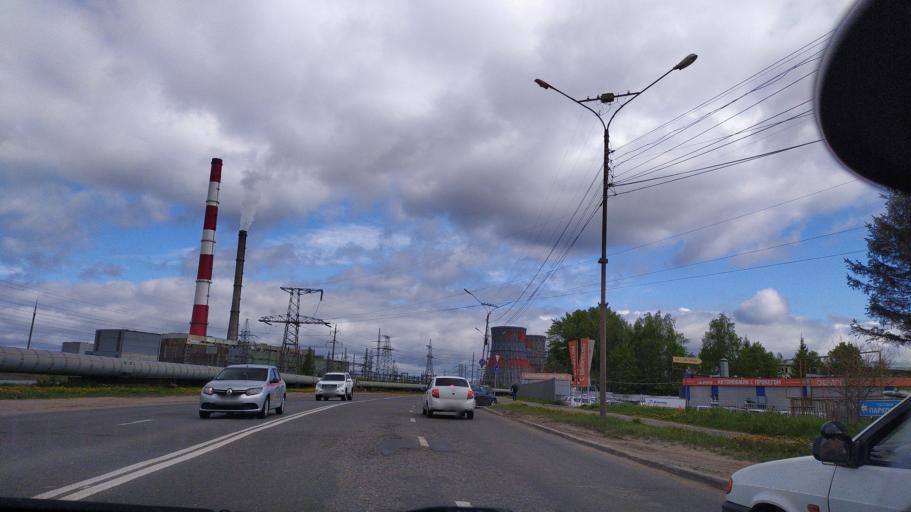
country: RU
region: Chuvashia
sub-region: Cheboksarskiy Rayon
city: Cheboksary
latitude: 56.1189
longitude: 47.3019
